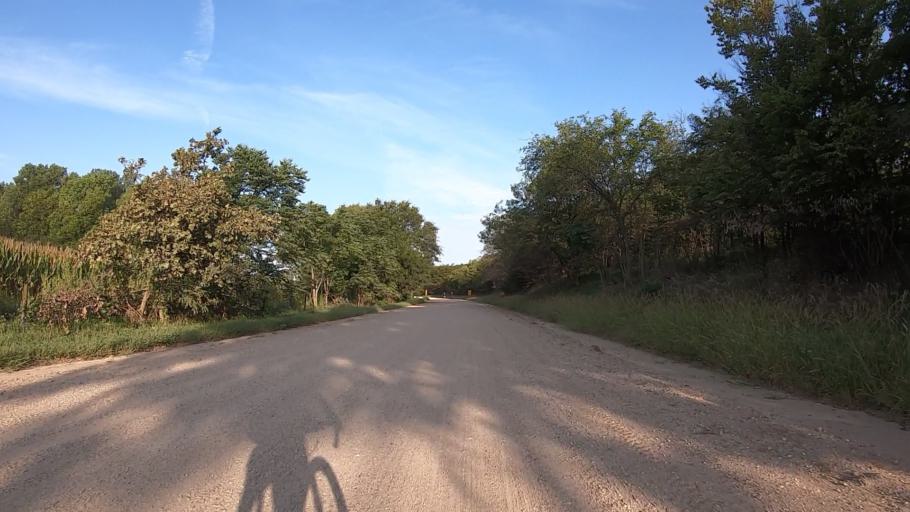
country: US
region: Kansas
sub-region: Marshall County
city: Blue Rapids
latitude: 39.7213
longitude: -96.7721
